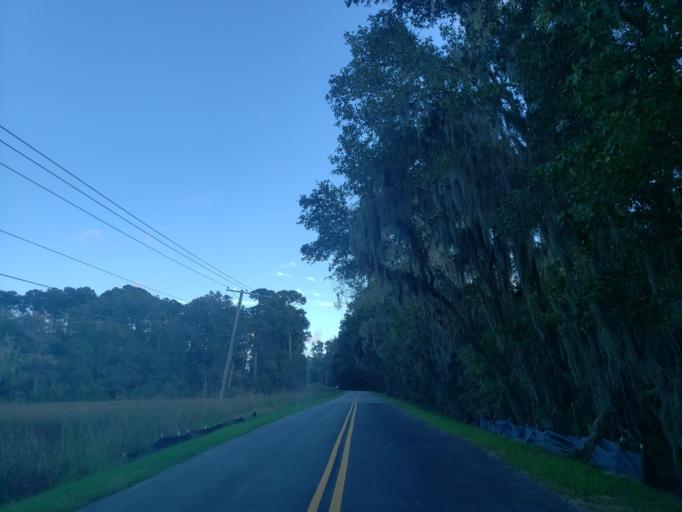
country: US
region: Georgia
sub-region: Chatham County
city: Georgetown
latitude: 31.9934
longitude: -81.2371
